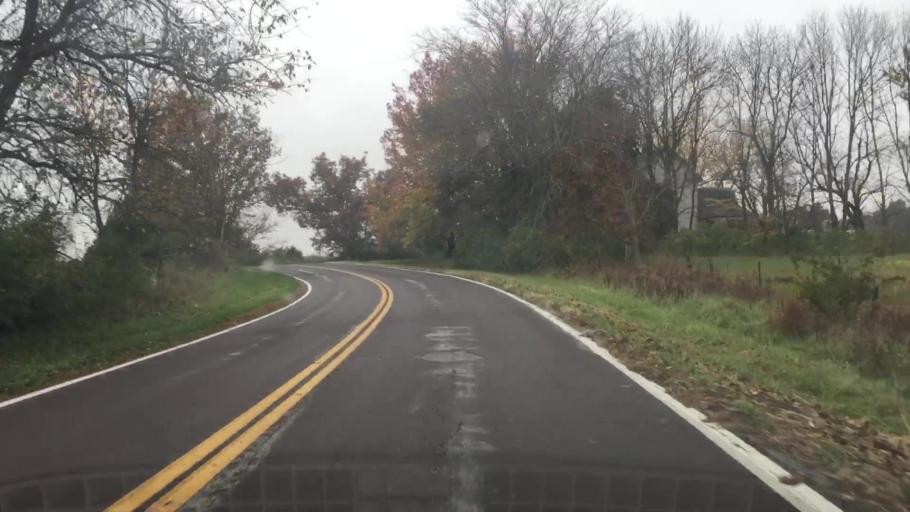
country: US
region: Missouri
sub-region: Callaway County
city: Fulton
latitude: 38.8360
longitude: -91.9205
